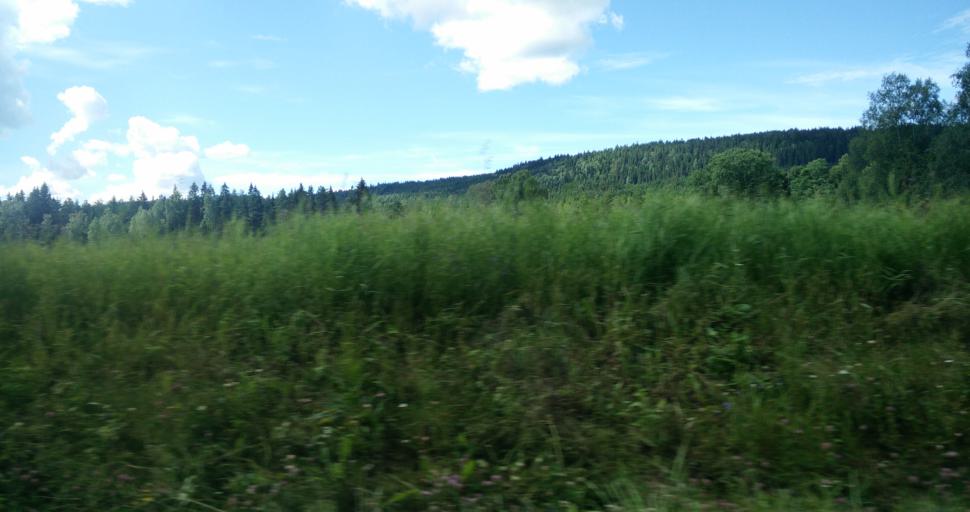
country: SE
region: Vaermland
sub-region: Hagfors Kommun
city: Ekshaerad
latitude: 60.0506
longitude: 13.4855
